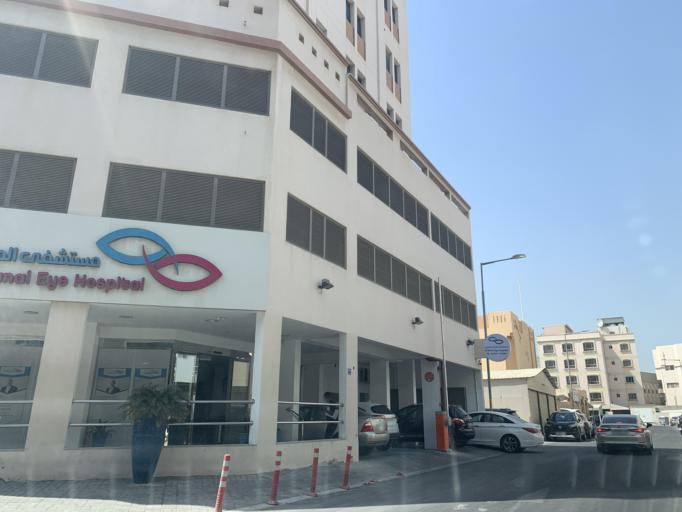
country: BH
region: Manama
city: Manama
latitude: 26.2083
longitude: 50.5774
